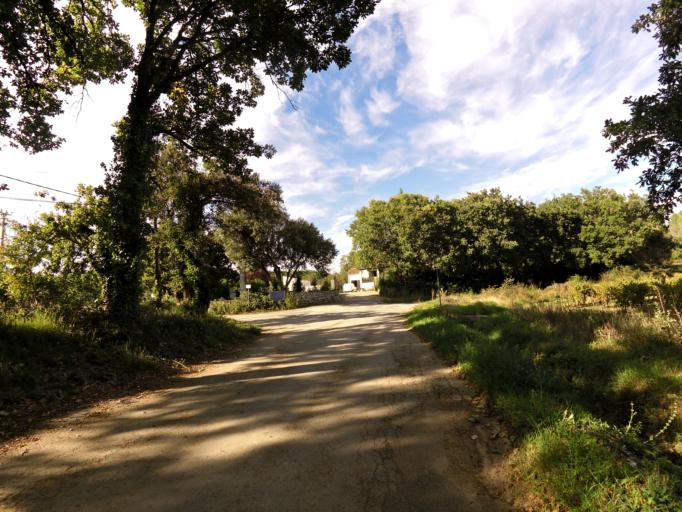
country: FR
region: Languedoc-Roussillon
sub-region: Departement du Gard
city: Villevieille
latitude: 43.8103
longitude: 4.0880
